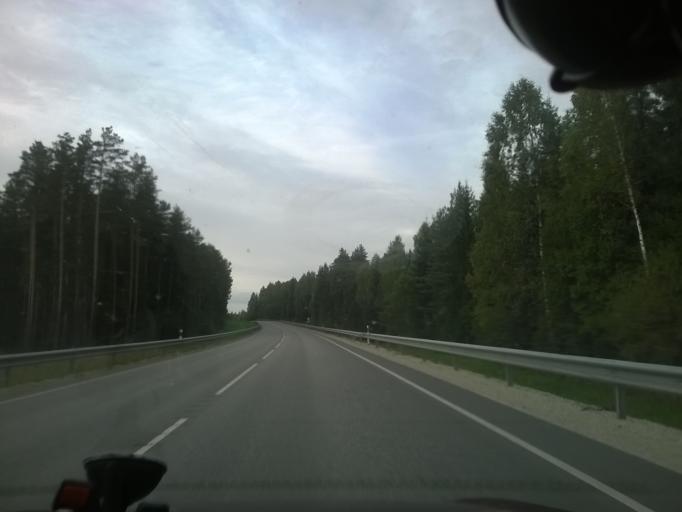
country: EE
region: Vorumaa
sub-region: Voru linn
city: Voru
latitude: 57.9634
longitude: 26.7913
